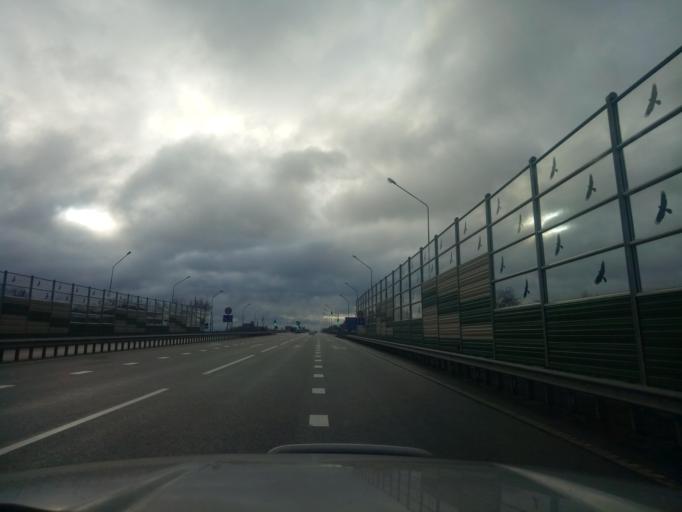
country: BY
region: Minsk
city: Slutsk
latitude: 53.2223
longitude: 27.5506
